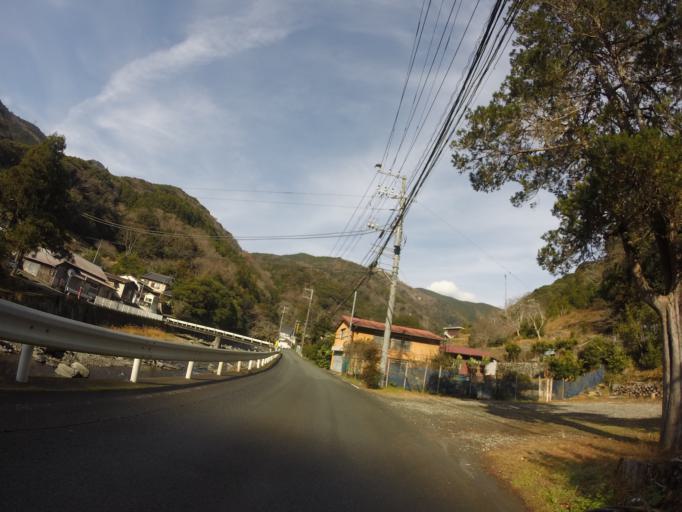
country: JP
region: Shizuoka
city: Heda
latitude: 34.8114
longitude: 138.8252
